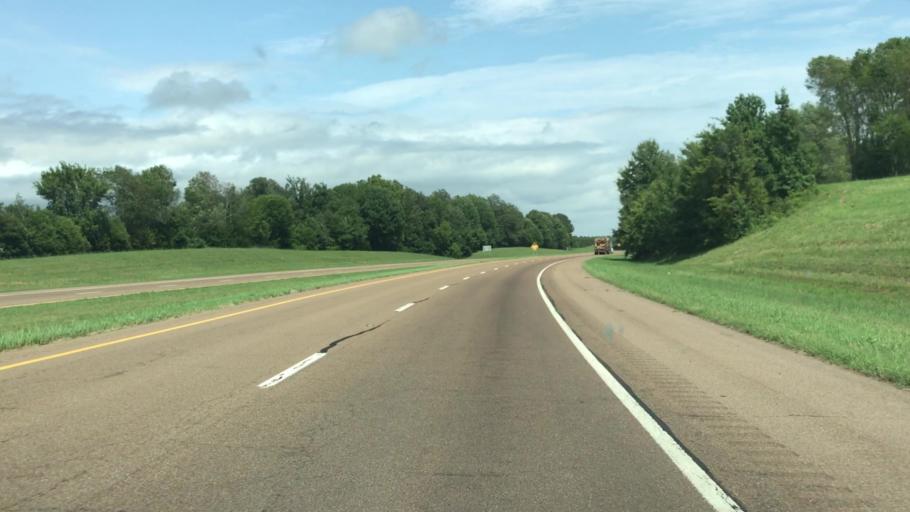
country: US
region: Tennessee
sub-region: Obion County
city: South Fulton
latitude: 36.4944
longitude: -88.9141
